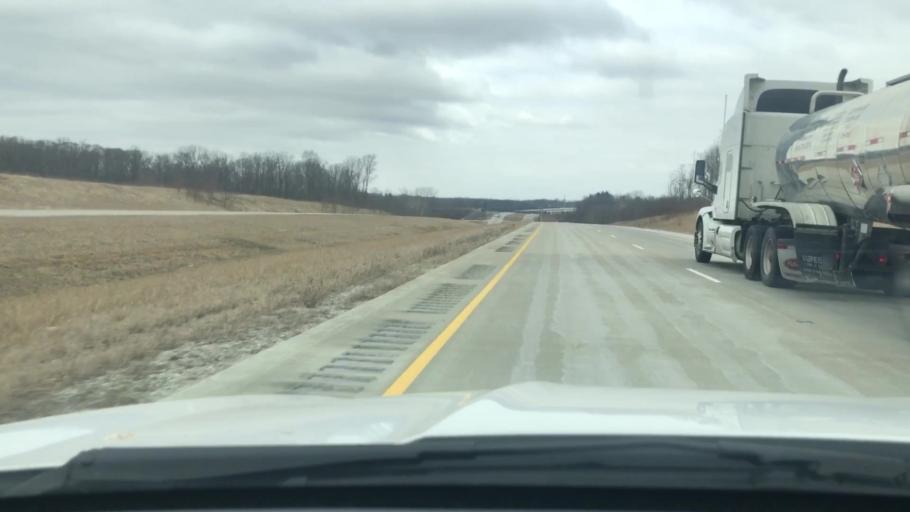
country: US
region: Indiana
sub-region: Carroll County
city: Delphi
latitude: 40.5860
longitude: -86.6506
